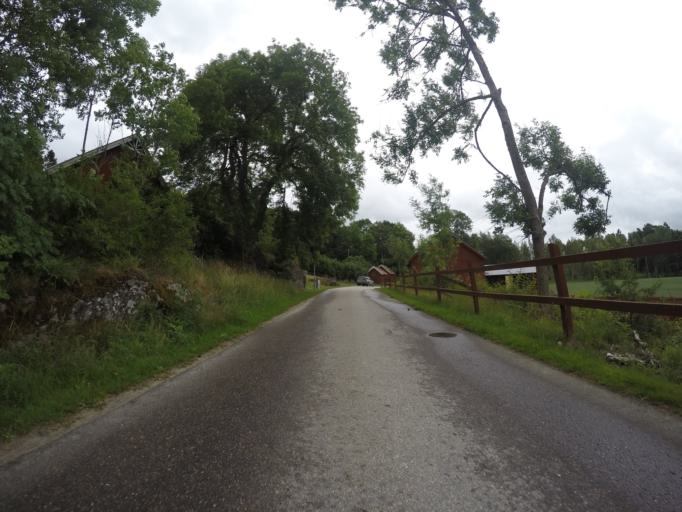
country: SE
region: Vaestra Goetaland
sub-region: Trollhattan
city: Sjuntorp
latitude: 58.1968
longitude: 12.2449
